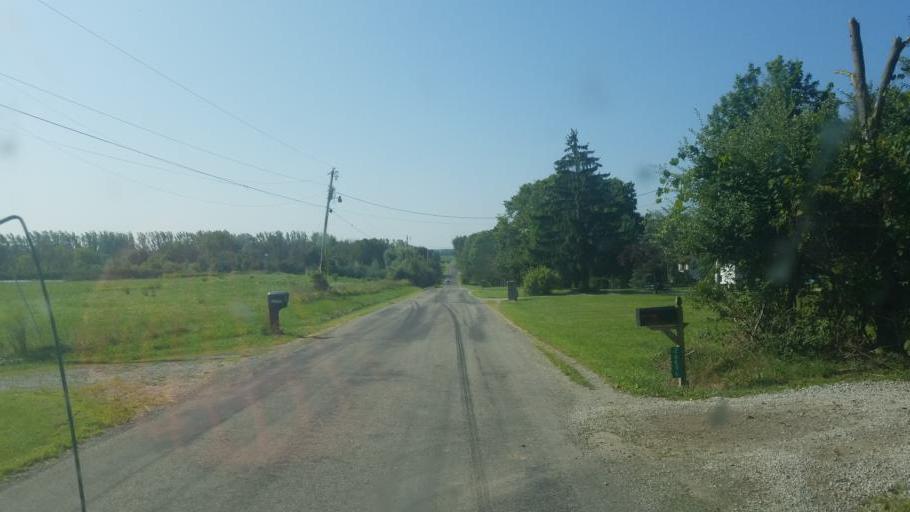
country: US
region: Ohio
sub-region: Lorain County
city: Wellington
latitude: 41.1063
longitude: -82.2006
